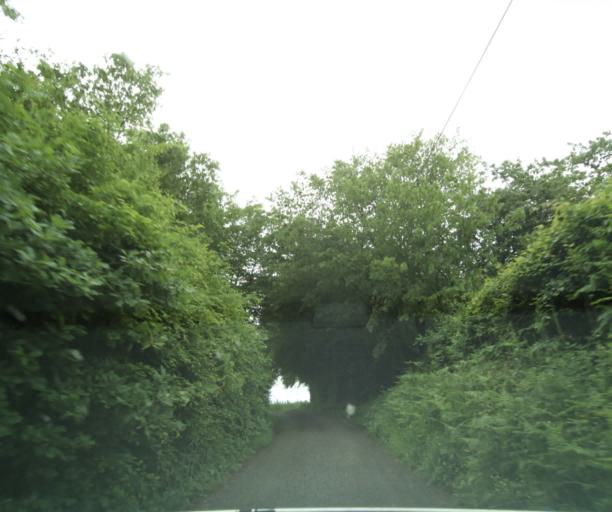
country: FR
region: Bourgogne
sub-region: Departement de Saone-et-Loire
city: Charolles
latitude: 46.4649
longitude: 4.3340
